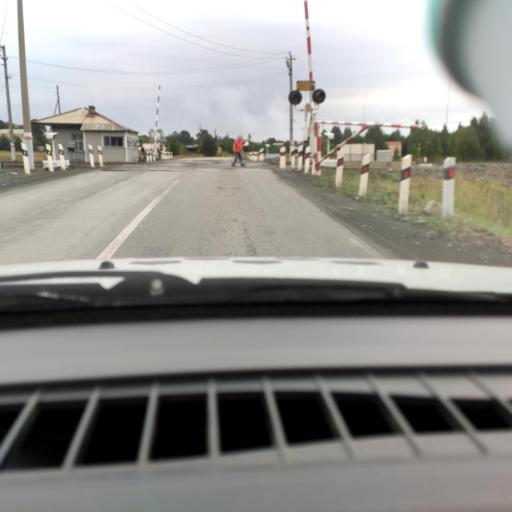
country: RU
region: Chelyabinsk
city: Karabash
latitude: 55.4459
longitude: 60.2229
